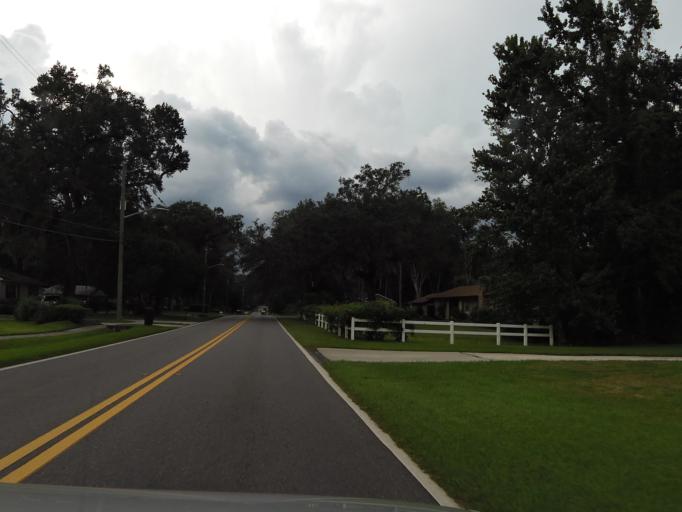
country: US
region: Florida
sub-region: Clay County
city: Bellair-Meadowbrook Terrace
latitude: 30.2848
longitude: -81.7586
